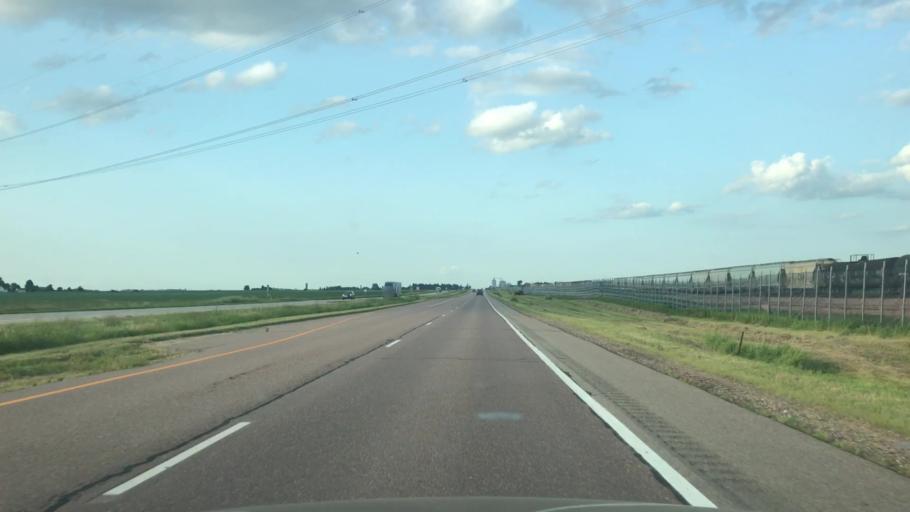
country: US
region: Minnesota
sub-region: Nobles County
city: Worthington
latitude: 43.6712
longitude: -95.5137
